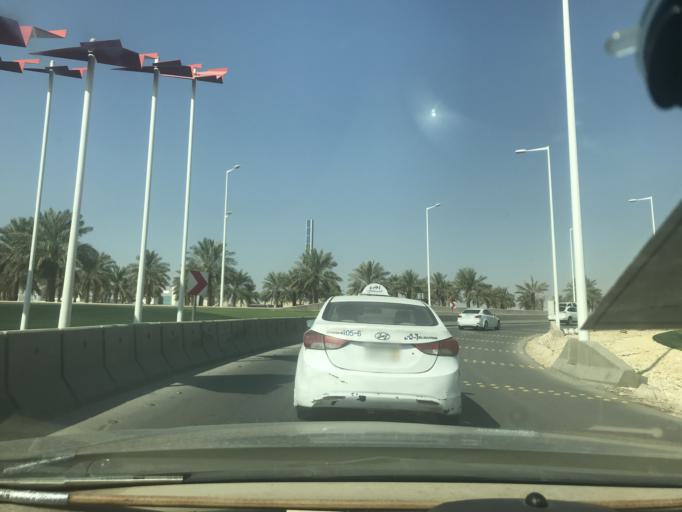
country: SA
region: Ar Riyad
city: Riyadh
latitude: 24.7271
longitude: 46.7082
